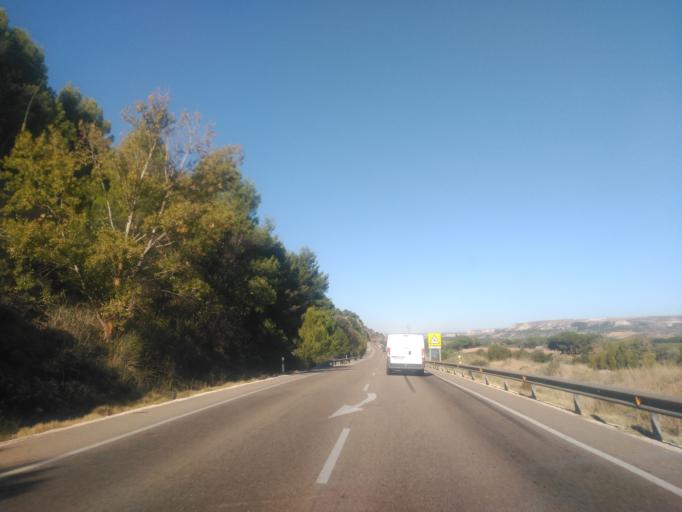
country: ES
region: Castille and Leon
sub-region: Provincia de Valladolid
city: Bocos de Duero
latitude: 41.6048
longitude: -4.0485
